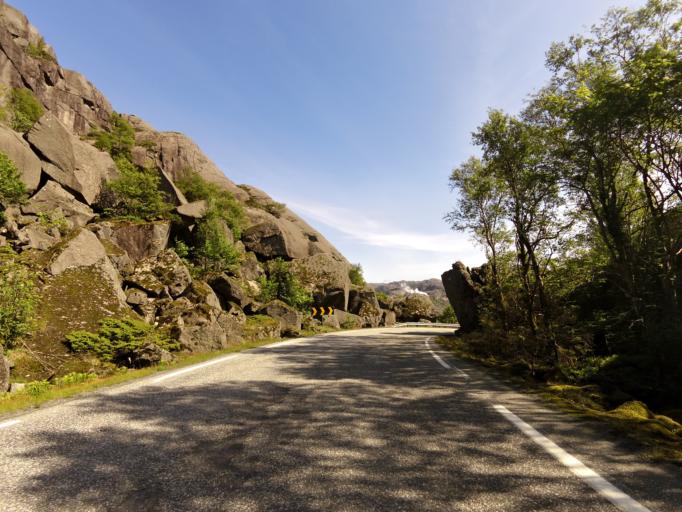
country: NO
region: Rogaland
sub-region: Sokndal
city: Hauge i Dalane
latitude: 58.3322
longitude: 6.3506
